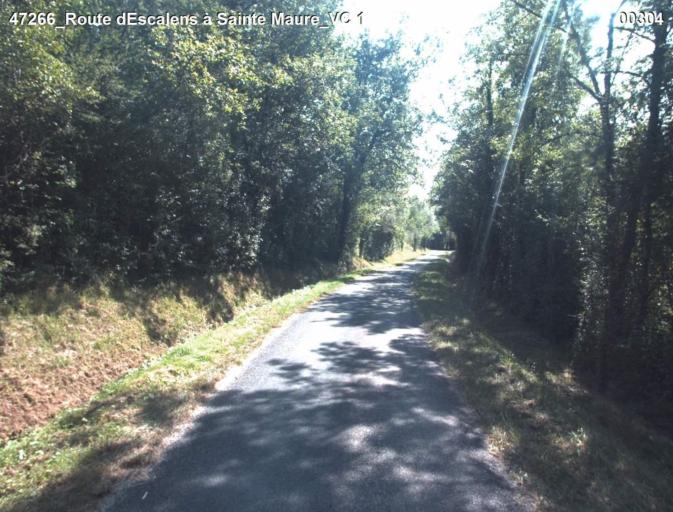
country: FR
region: Aquitaine
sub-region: Departement des Landes
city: Gabarret
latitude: 44.0103
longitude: 0.0636
